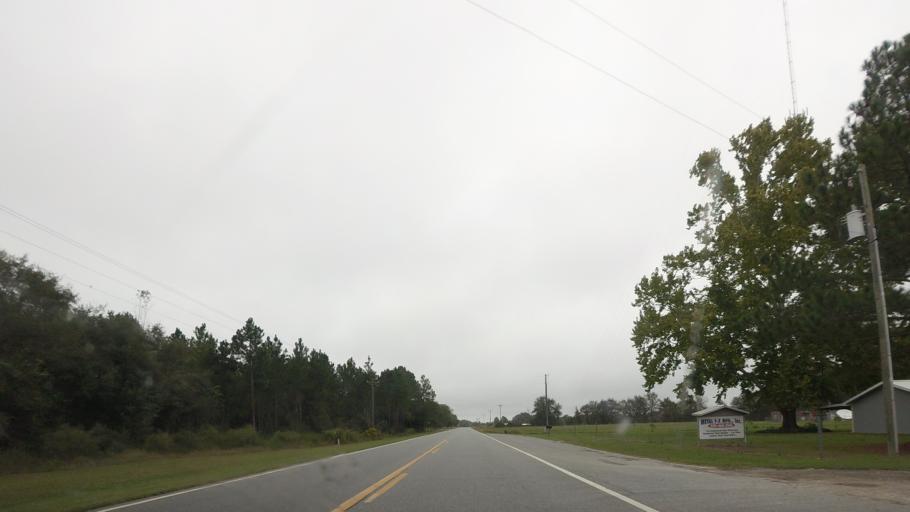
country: US
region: Georgia
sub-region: Berrien County
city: Enigma
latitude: 31.4689
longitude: -83.2378
